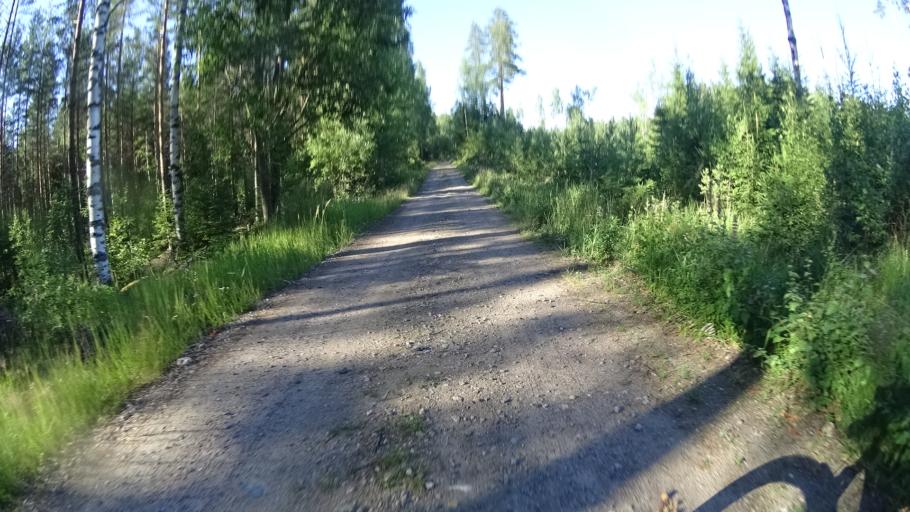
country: FI
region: Uusimaa
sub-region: Helsinki
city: Karkkila
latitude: 60.6536
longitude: 24.1313
